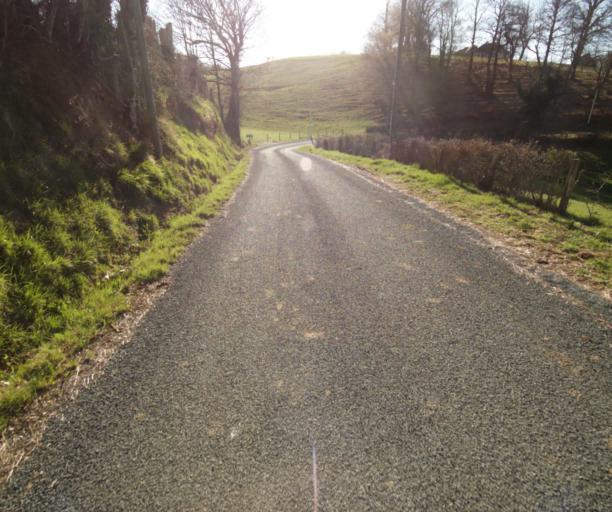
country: FR
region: Limousin
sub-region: Departement de la Correze
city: Seilhac
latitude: 45.3634
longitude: 1.7583
